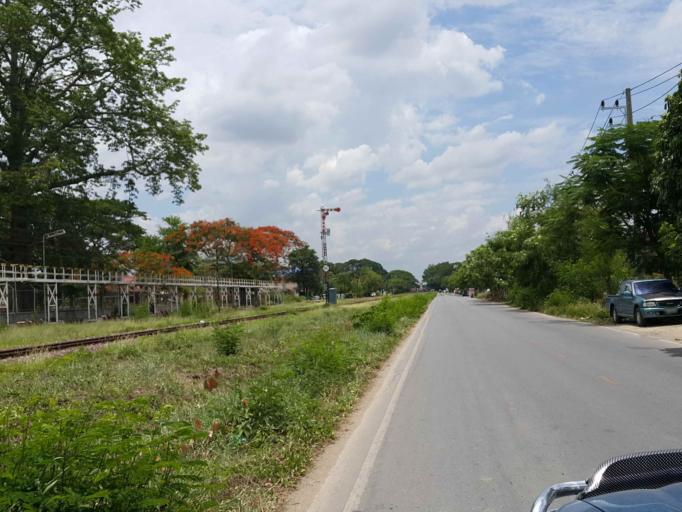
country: TH
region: Chiang Mai
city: Chiang Mai
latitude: 18.7708
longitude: 99.0173
